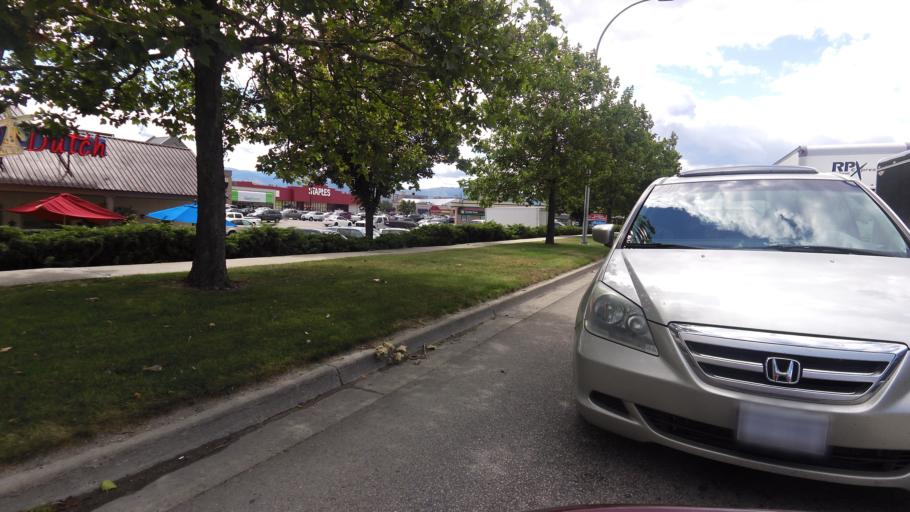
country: CA
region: British Columbia
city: Kelowna
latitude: 49.8840
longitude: -119.4297
